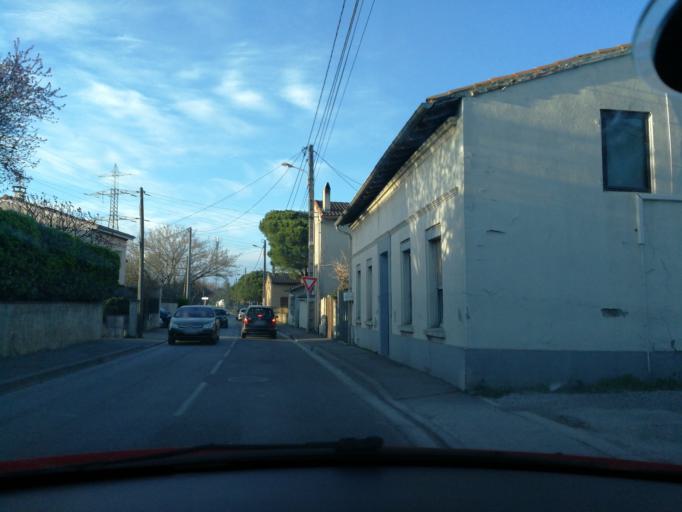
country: FR
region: Midi-Pyrenees
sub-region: Departement de la Haute-Garonne
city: Blagnac
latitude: 43.6466
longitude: 1.4145
